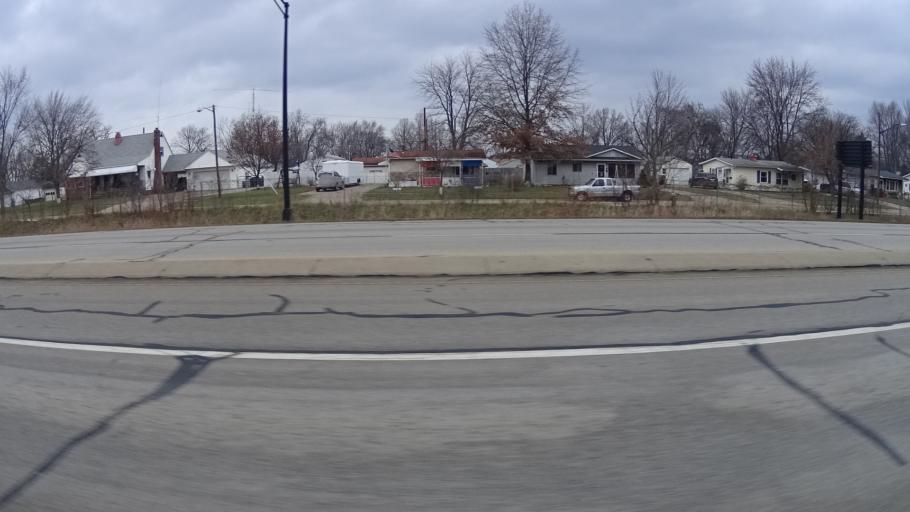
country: US
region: Ohio
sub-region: Lorain County
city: Elyria
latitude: 41.3827
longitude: -82.1079
